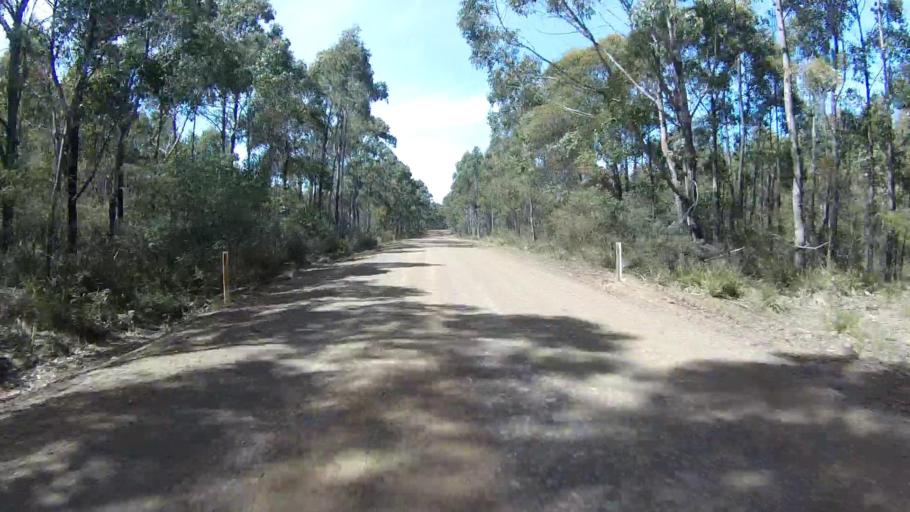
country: AU
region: Tasmania
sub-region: Sorell
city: Sorell
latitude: -42.6755
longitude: 147.7293
